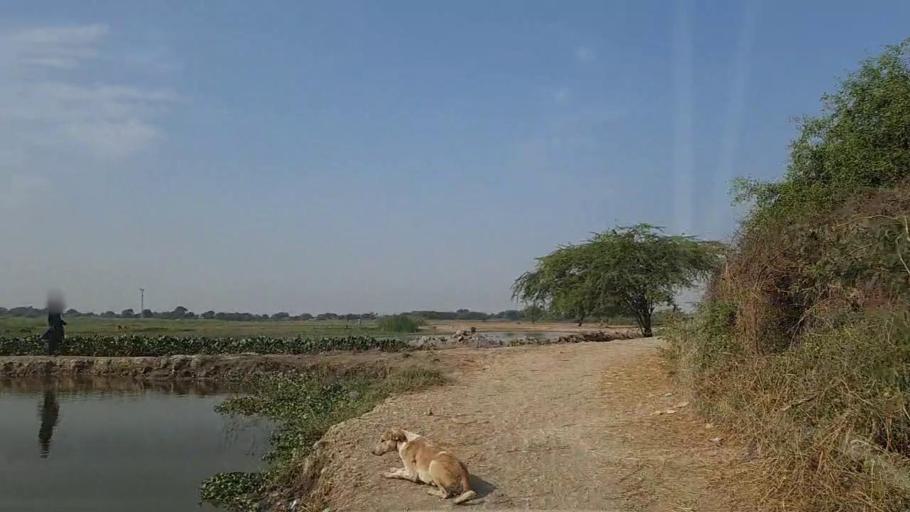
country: PK
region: Sindh
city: Mirpur Batoro
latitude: 24.7185
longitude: 68.2195
